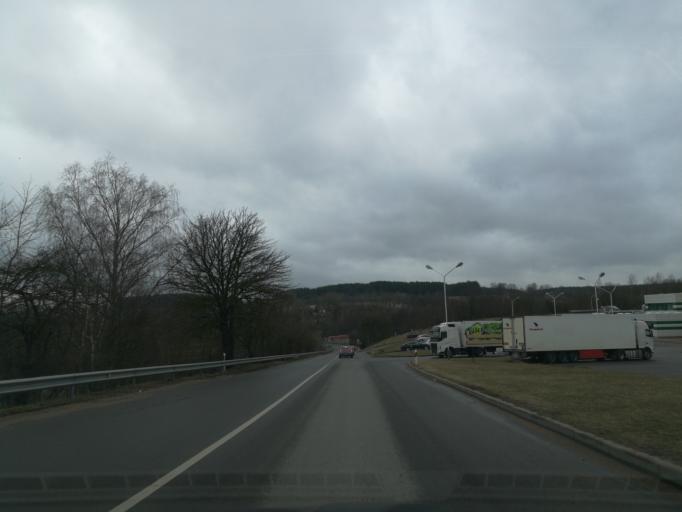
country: LT
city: Grigiskes
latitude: 54.6476
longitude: 25.1236
